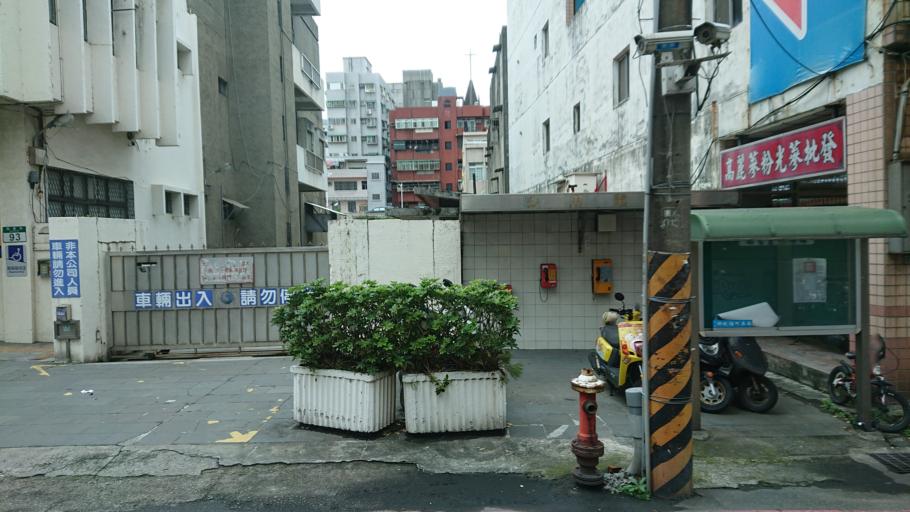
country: TW
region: Taiwan
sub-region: Taoyuan
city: Taoyuan
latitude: 24.9546
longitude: 121.3504
